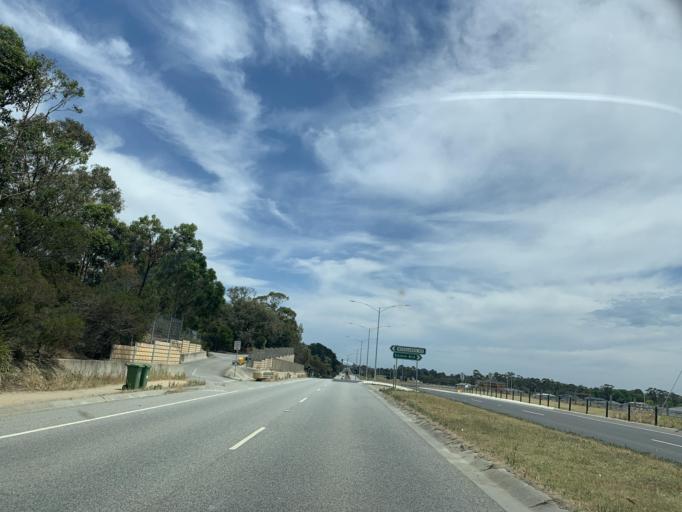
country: AU
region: Victoria
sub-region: Casey
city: Cranbourne South
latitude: -38.1301
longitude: 145.2366
